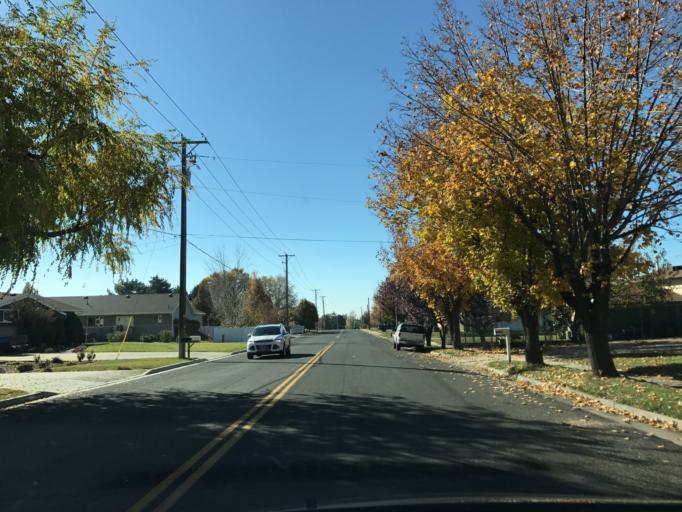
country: US
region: Utah
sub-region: Davis County
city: Layton
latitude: 41.0729
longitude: -111.9609
